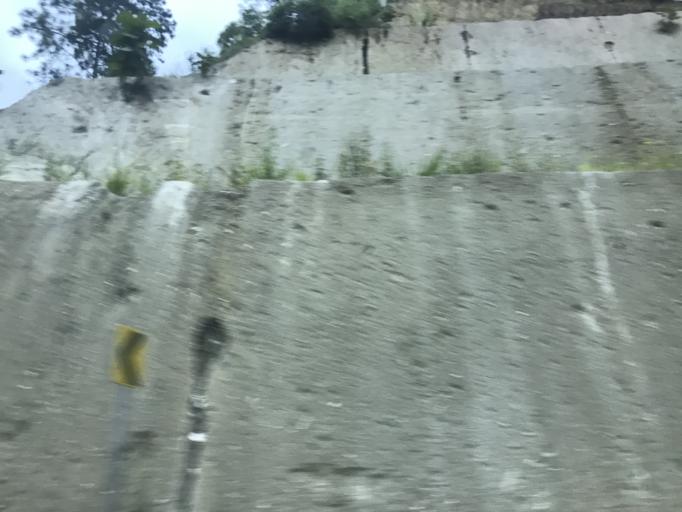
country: GT
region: Chimaltenango
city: El Tejar
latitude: 14.6389
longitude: -90.7918
